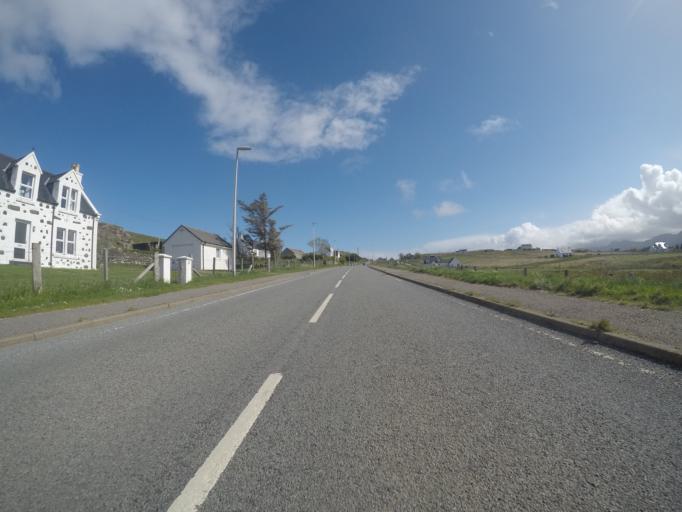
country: GB
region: Scotland
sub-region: Highland
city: Portree
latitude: 57.6240
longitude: -6.2022
